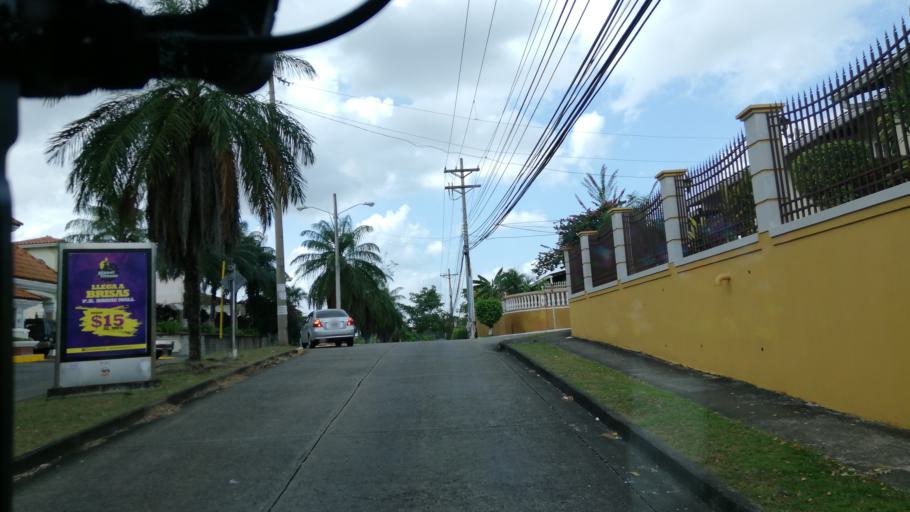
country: PA
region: Panama
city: San Miguelito
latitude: 9.0648
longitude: -79.4572
